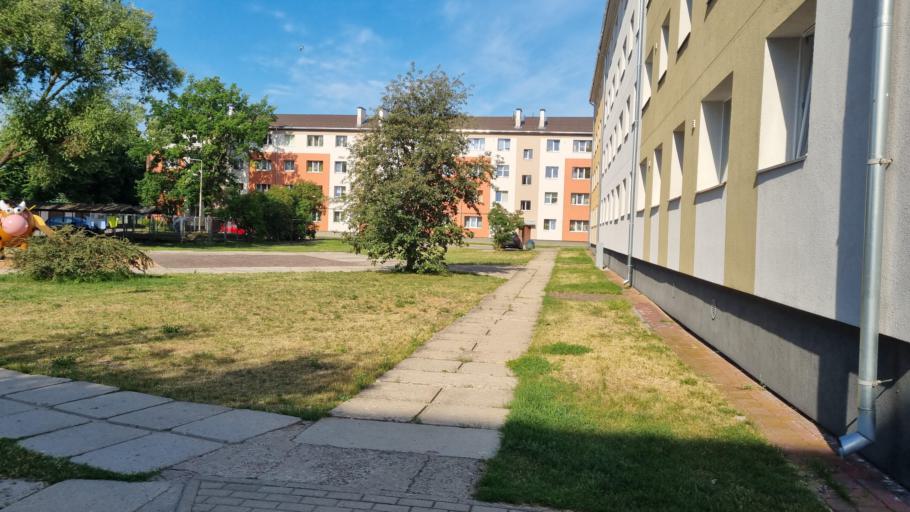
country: LV
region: Ventspils
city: Ventspils
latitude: 57.3894
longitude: 21.5720
